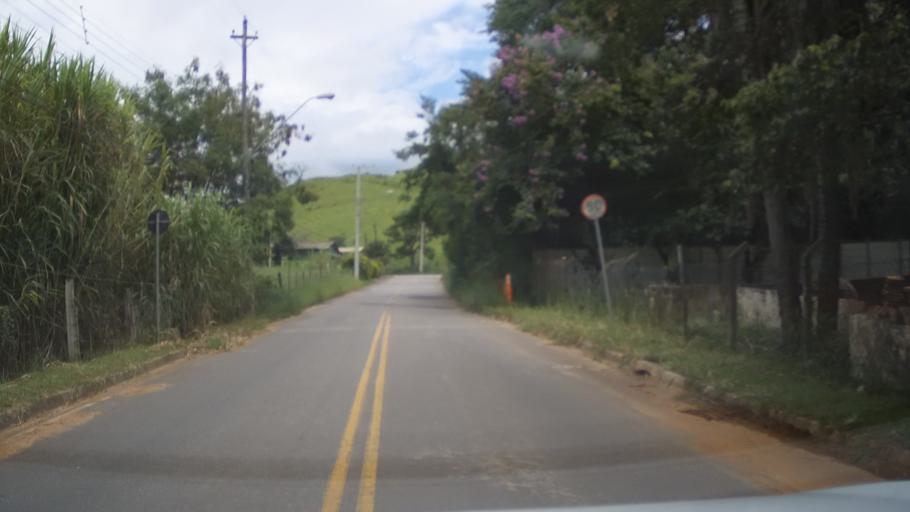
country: BR
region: Sao Paulo
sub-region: Vinhedo
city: Vinhedo
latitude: -23.0550
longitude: -47.0330
